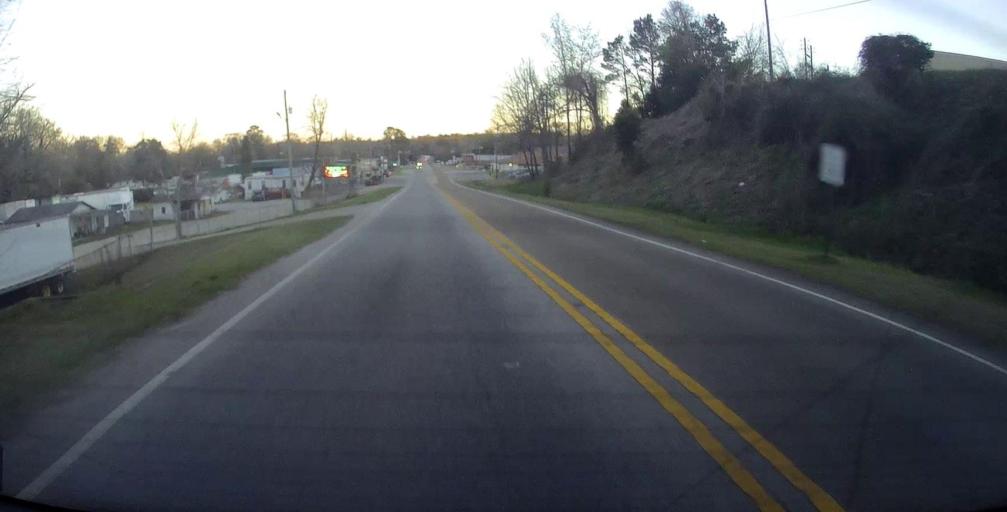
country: US
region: Alabama
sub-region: Russell County
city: Phenix City
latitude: 32.4811
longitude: -85.0285
